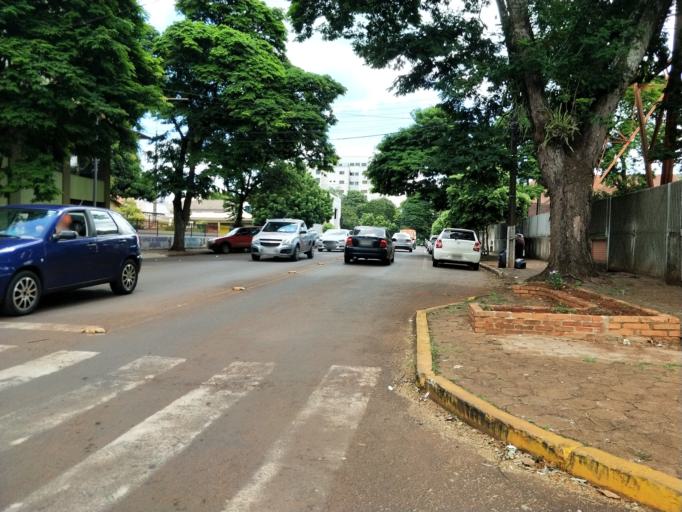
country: BR
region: Parana
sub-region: Marechal Candido Rondon
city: Marechal Candido Rondon
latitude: -24.5588
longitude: -54.0574
